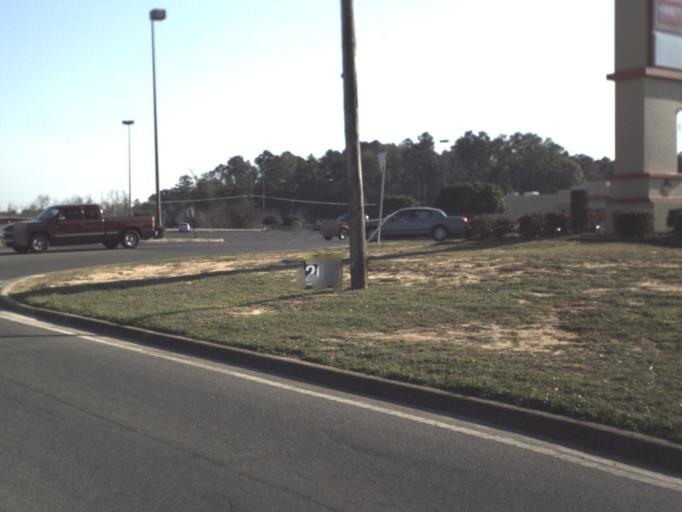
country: US
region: Florida
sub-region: Jackson County
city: Marianna
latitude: 30.7629
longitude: -85.2006
